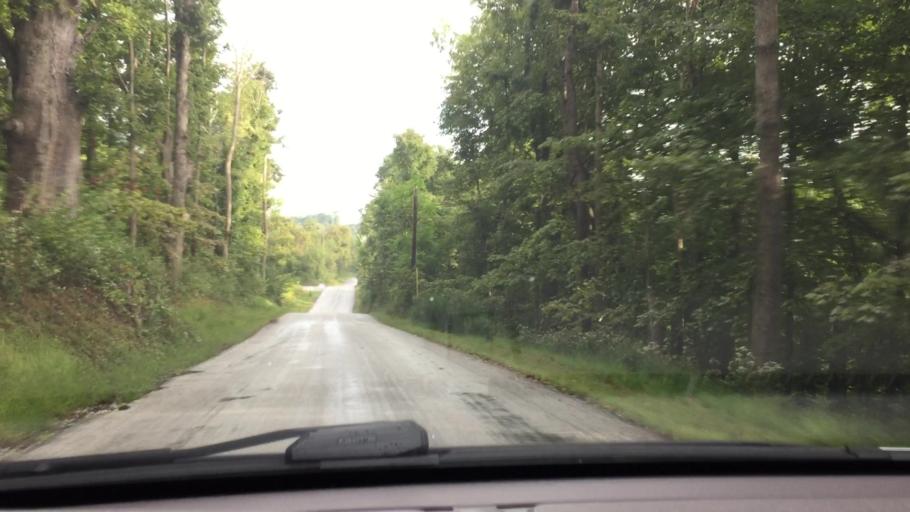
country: US
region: Pennsylvania
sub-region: Washington County
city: McGovern
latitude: 40.1905
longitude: -80.1676
